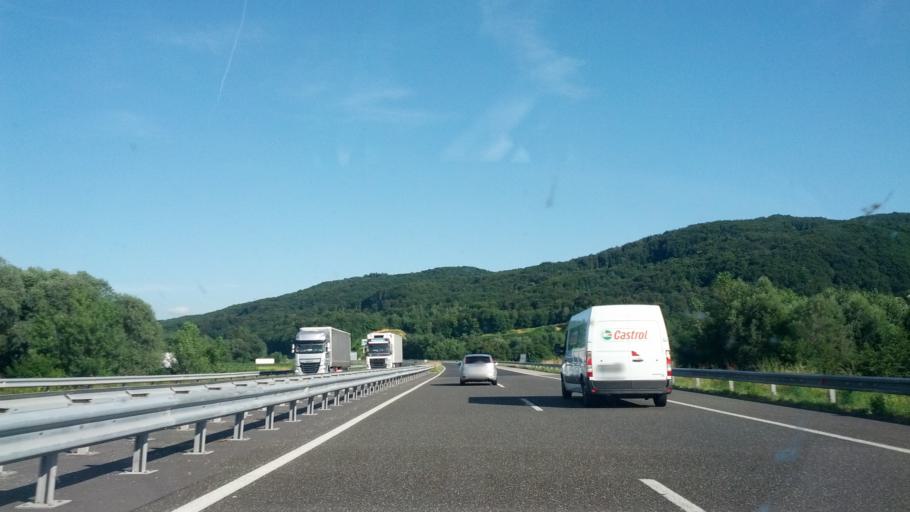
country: SI
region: Brezice
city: Brezice
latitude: 45.8839
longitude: 15.6201
